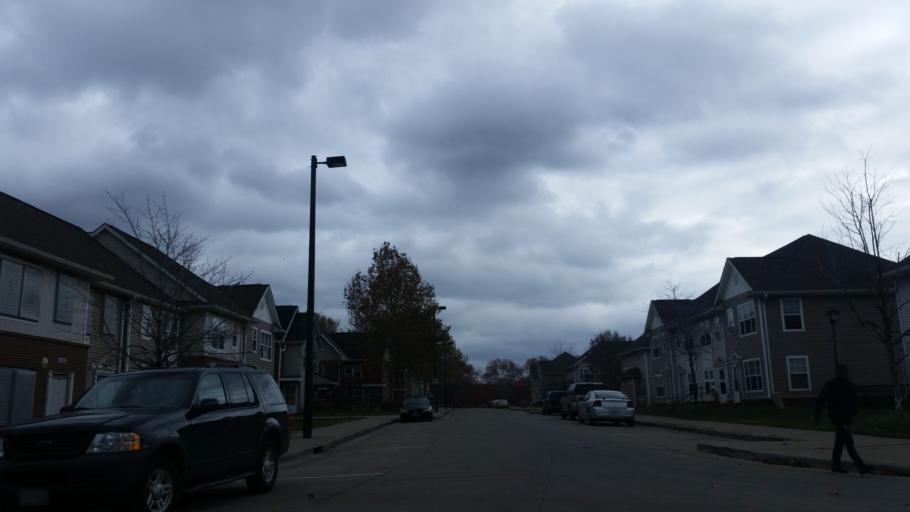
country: US
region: Ohio
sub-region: Cuyahoga County
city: Cleveland
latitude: 41.4959
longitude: -81.6542
